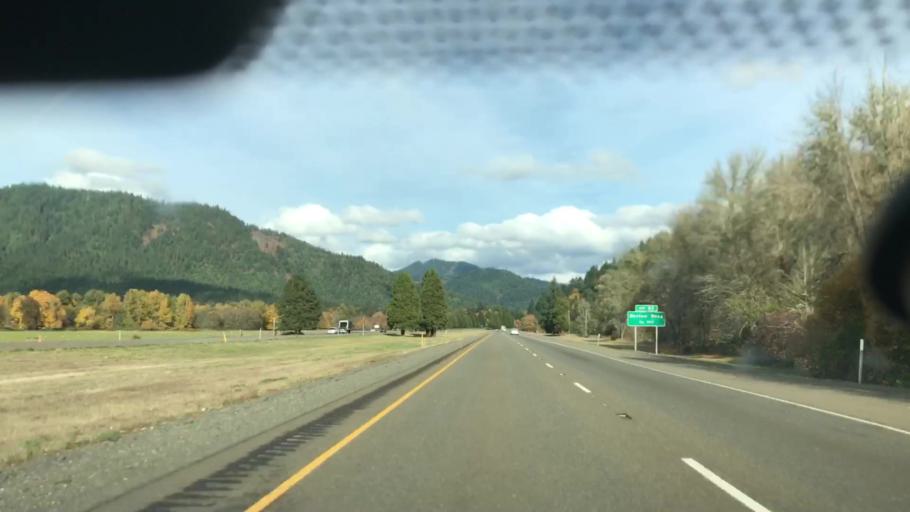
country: US
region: Oregon
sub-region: Douglas County
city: Canyonville
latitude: 42.7599
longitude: -123.3477
